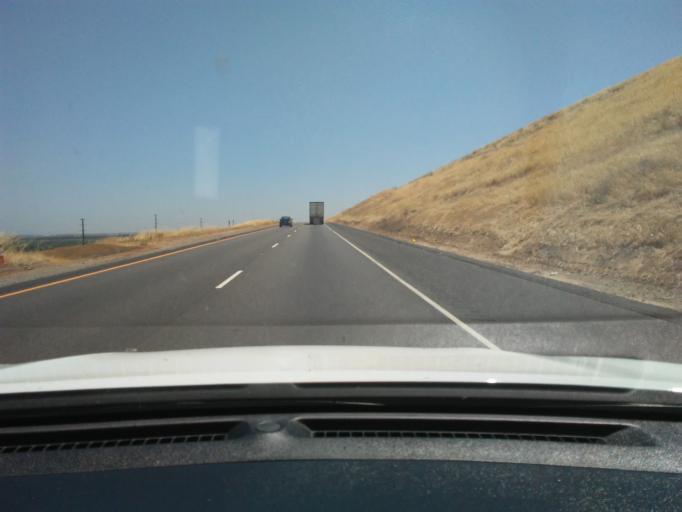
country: US
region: California
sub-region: Stanislaus County
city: Patterson
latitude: 37.4580
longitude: -121.1762
